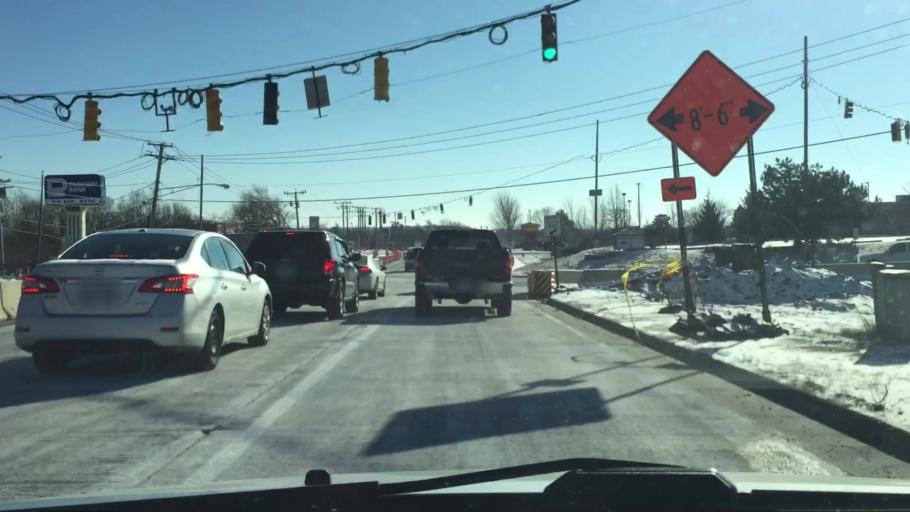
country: US
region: Illinois
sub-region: Kane County
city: West Dundee
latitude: 42.1083
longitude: -88.2942
